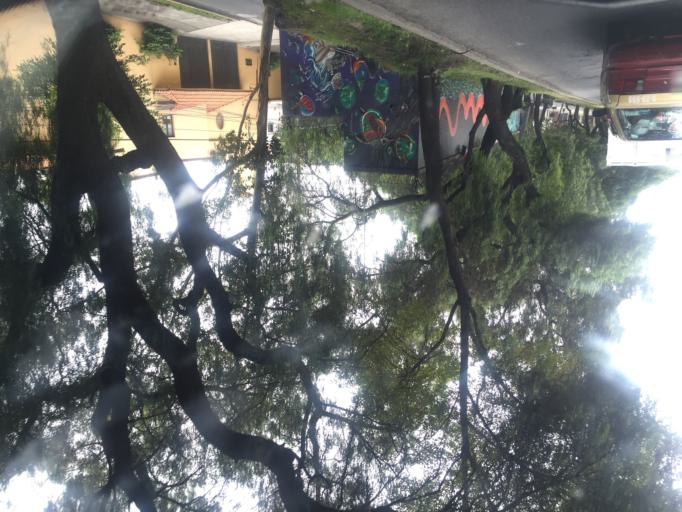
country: MX
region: Mexico City
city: Tlalpan
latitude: 19.2840
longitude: -99.1609
